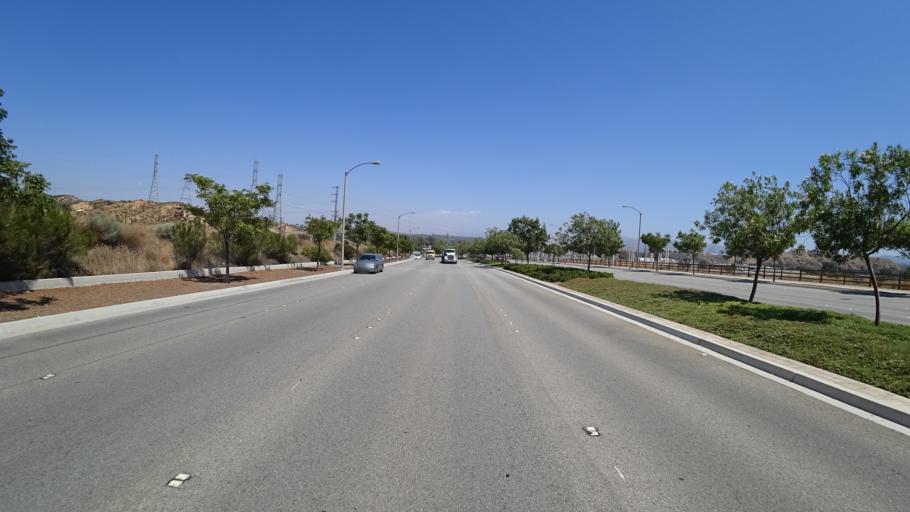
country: US
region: California
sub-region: Los Angeles County
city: Valencia
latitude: 34.4415
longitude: -118.5901
